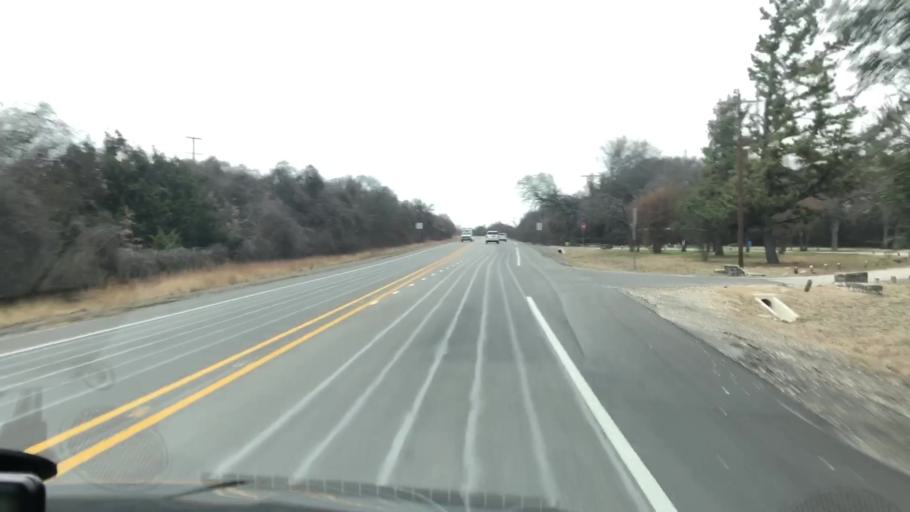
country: US
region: Texas
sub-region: Hamilton County
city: Hico
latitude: 32.0913
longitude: -98.1048
